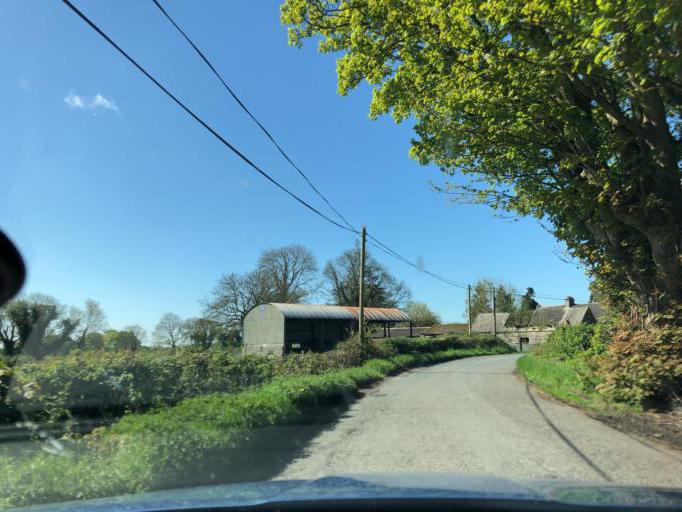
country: IE
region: Connaught
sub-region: County Galway
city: Portumna
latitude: 53.1794
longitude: -8.1770
